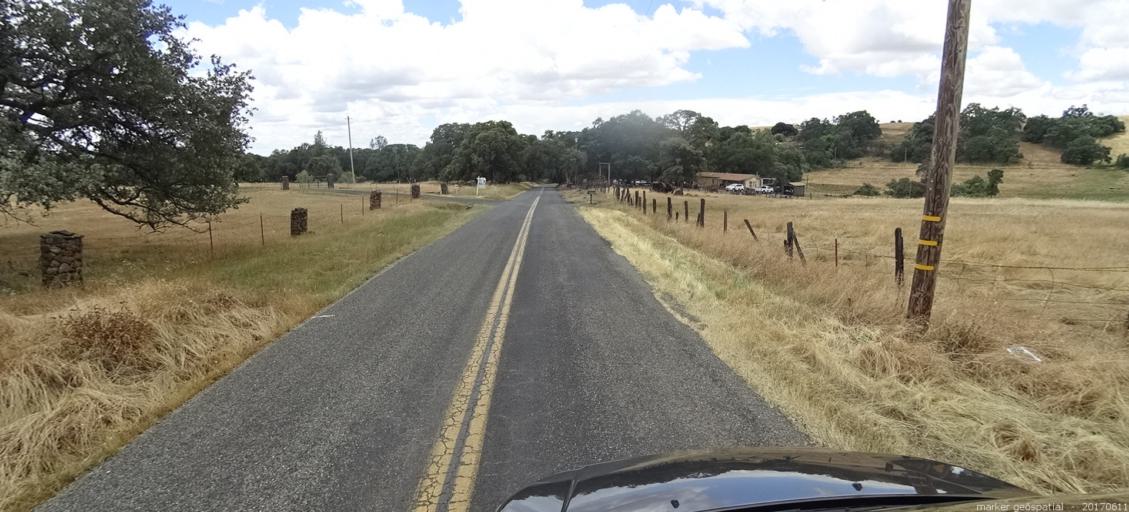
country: US
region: California
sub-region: Butte County
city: Oroville
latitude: 39.6045
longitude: -121.5318
